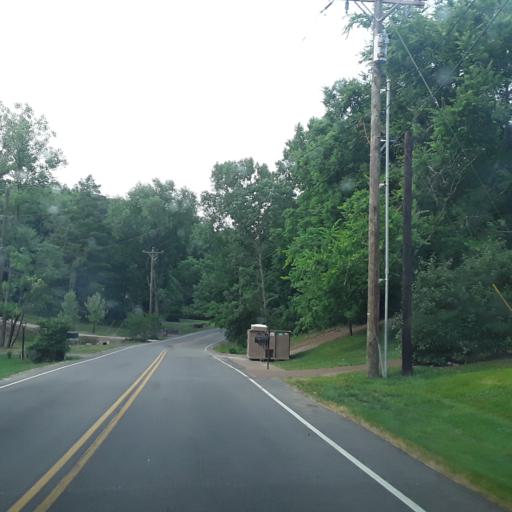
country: US
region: Tennessee
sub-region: Williamson County
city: Brentwood
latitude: 36.0515
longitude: -86.7815
